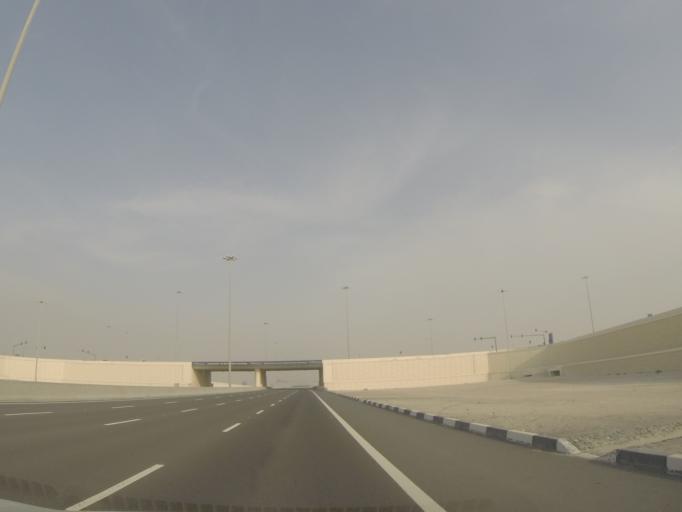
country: AE
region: Abu Dhabi
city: Abu Dhabi
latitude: 24.7708
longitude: 54.7180
